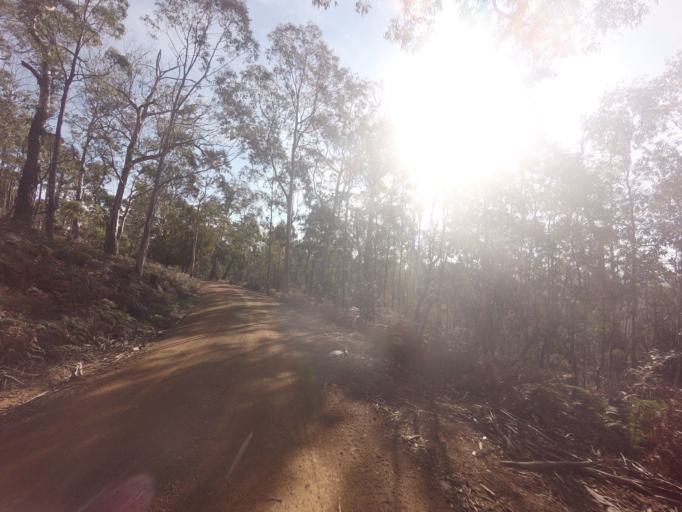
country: AU
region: Tasmania
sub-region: Sorell
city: Sorell
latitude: -42.5224
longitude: 147.4651
